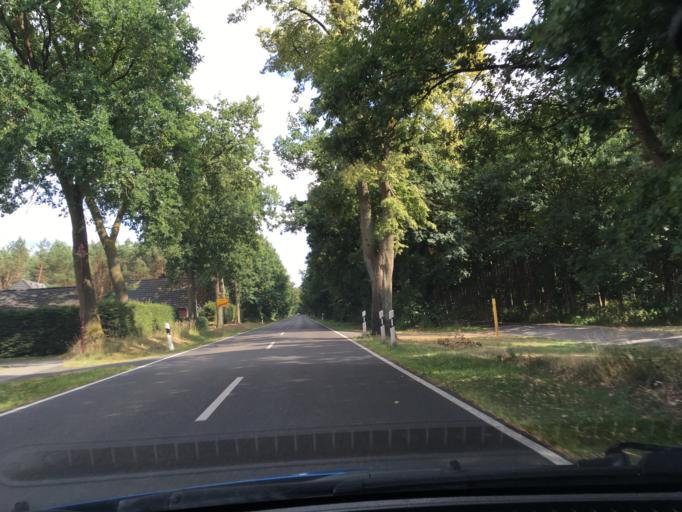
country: DE
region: Mecklenburg-Vorpommern
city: Lubtheen
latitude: 53.2945
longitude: 11.0878
